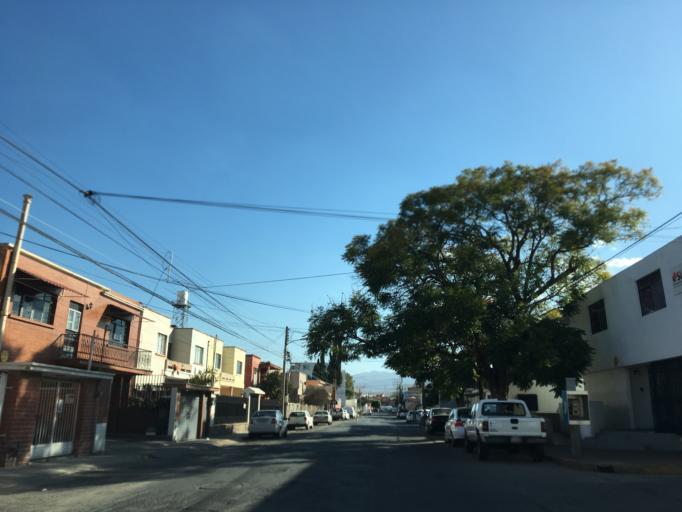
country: MX
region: San Luis Potosi
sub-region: San Luis Potosi
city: San Luis Potosi
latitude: 22.1472
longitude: -100.9926
